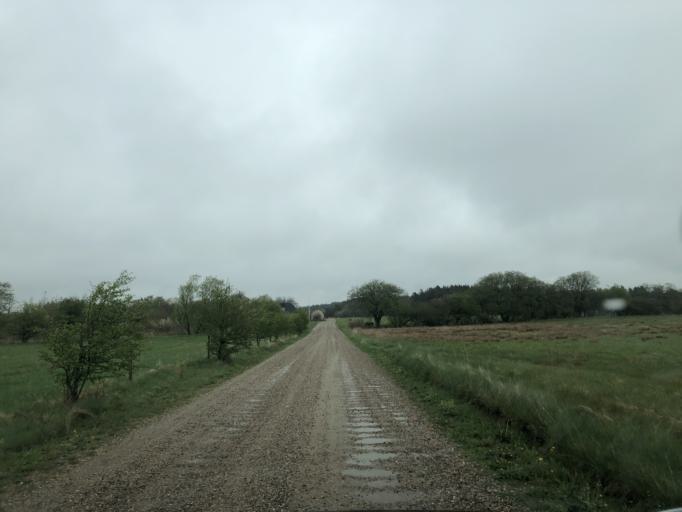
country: DK
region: Central Jutland
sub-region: Lemvig Kommune
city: Lemvig
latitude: 56.4429
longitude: 8.3775
